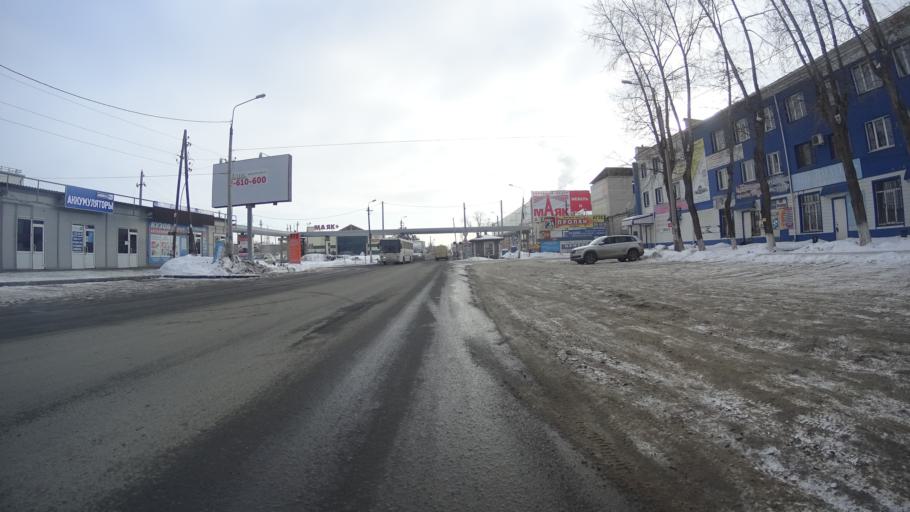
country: RU
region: Chelyabinsk
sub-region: Gorod Chelyabinsk
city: Chelyabinsk
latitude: 55.1212
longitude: 61.3860
